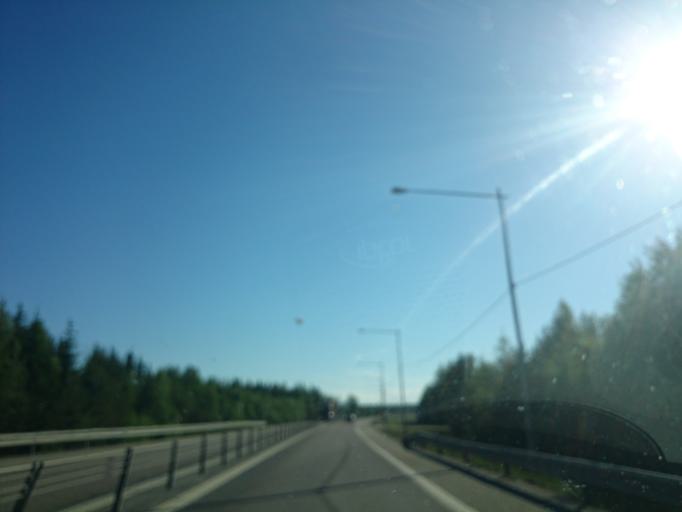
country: SE
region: Vaesternorrland
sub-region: Timra Kommun
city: Soraker
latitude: 62.5189
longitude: 17.4652
